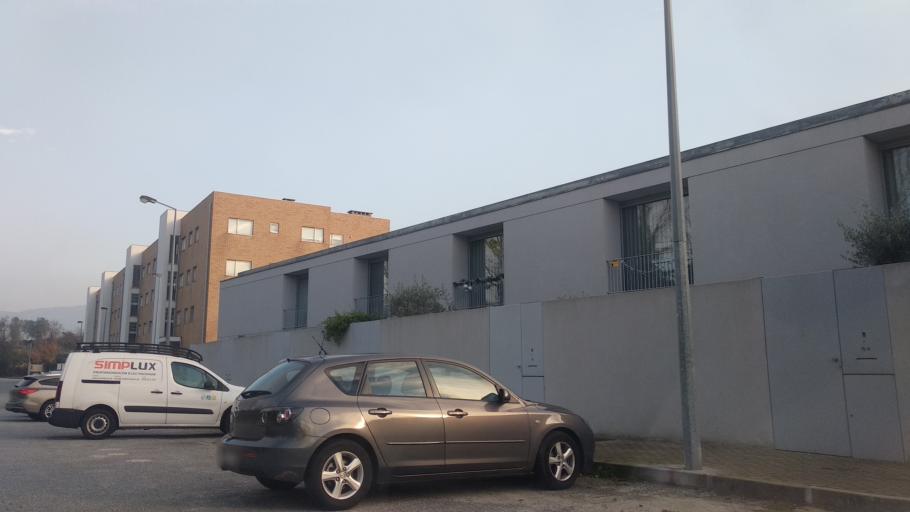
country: PT
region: Braga
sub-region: Braga
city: Adaufe
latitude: 41.5657
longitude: -8.3837
